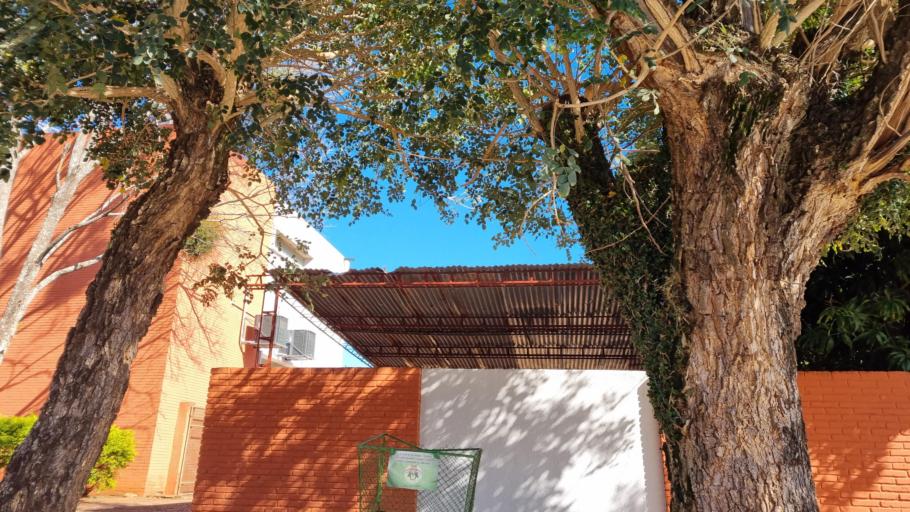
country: PY
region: Misiones
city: San Juan Bautista
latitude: -26.6684
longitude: -57.1415
